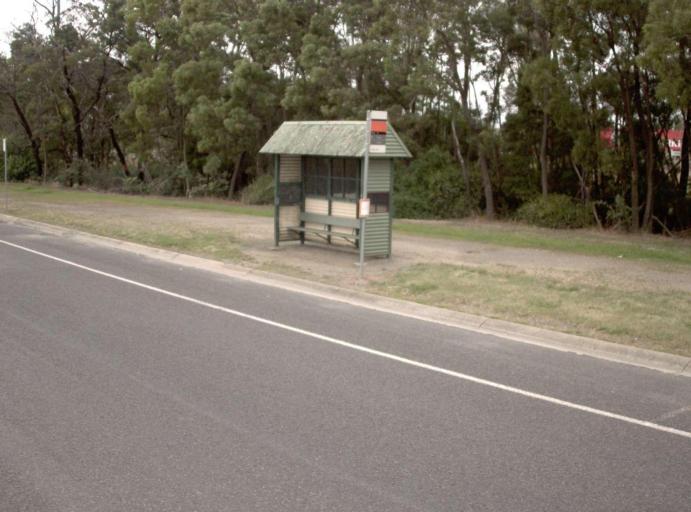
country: AU
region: Victoria
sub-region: Latrobe
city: Morwell
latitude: -38.2338
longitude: 146.3845
